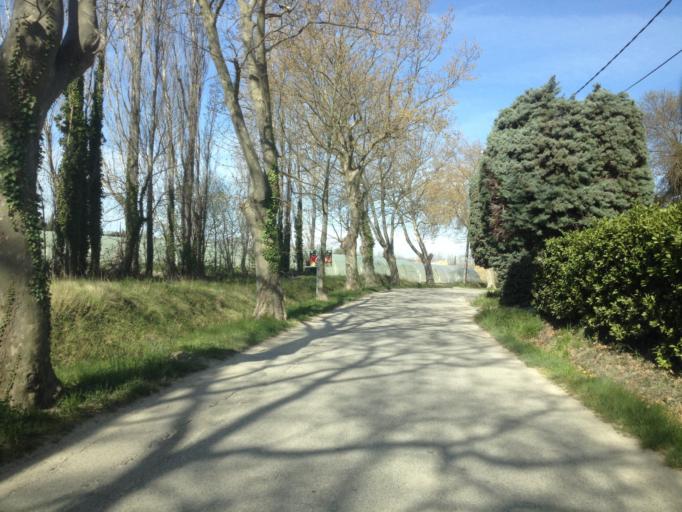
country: FR
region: Provence-Alpes-Cote d'Azur
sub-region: Departement du Vaucluse
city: Caderousse
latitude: 44.1004
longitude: 4.7628
